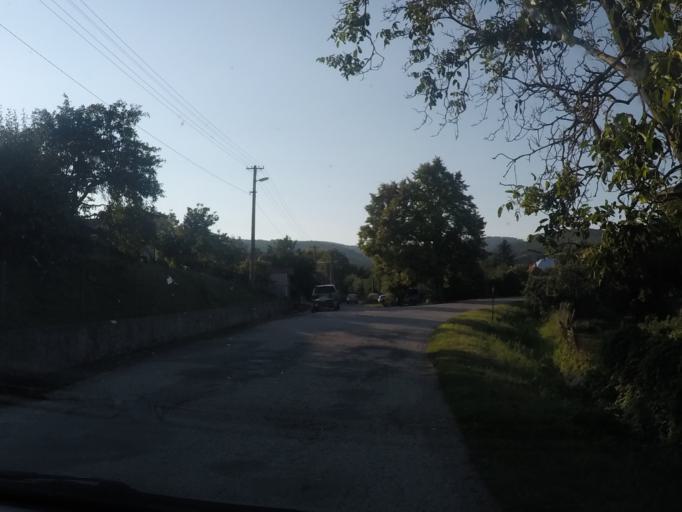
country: SK
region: Nitriansky
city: Zlate Moravce
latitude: 48.4617
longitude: 18.3157
